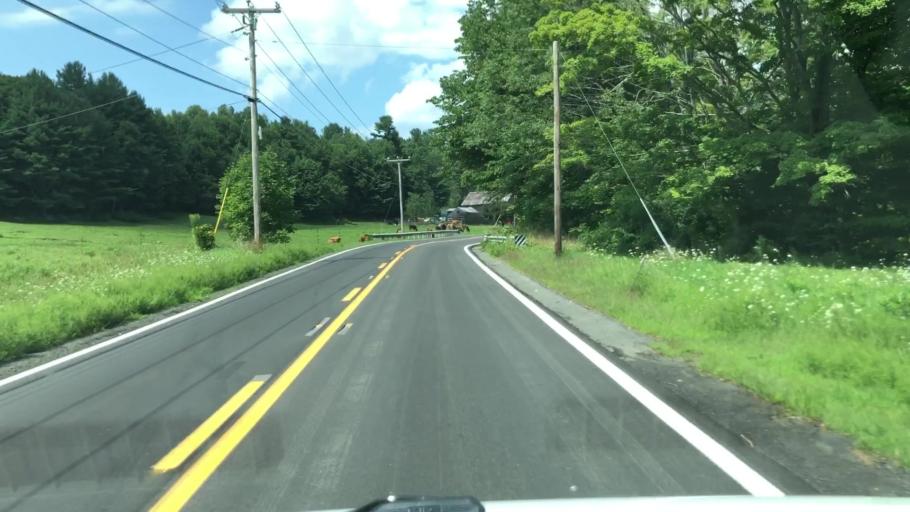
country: US
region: Massachusetts
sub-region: Franklin County
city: Ashfield
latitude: 42.5187
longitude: -72.7810
